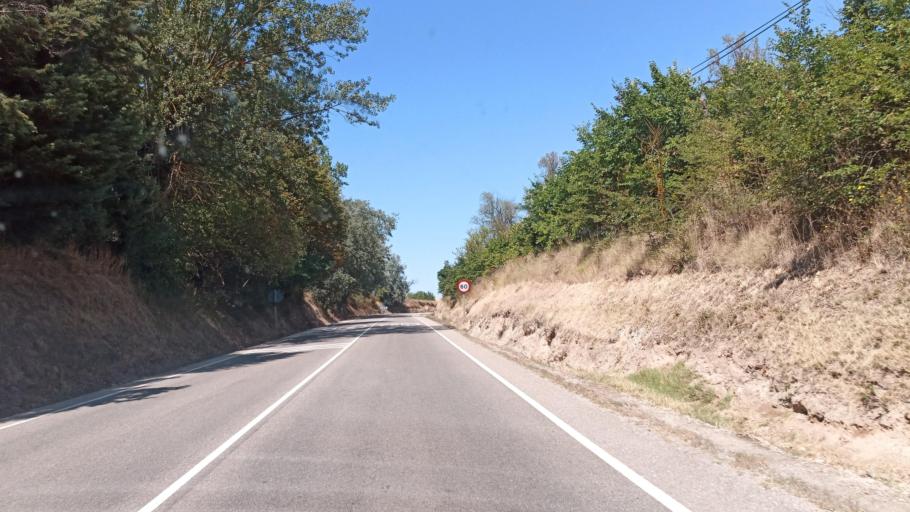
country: ES
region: Castille and Leon
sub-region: Provincia de Burgos
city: Briviesca
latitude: 42.5573
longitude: -3.3281
